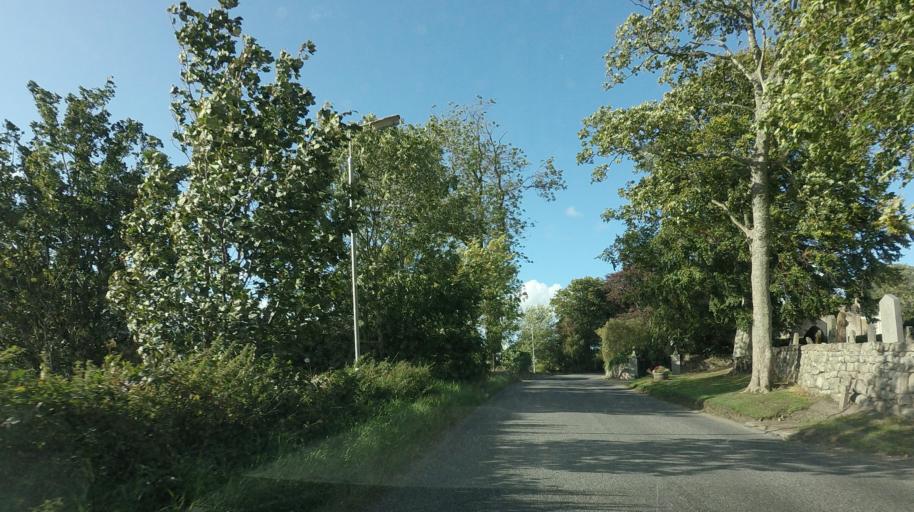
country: GB
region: Scotland
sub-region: Aberdeenshire
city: Kemnay
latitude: 57.1378
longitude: -2.4326
